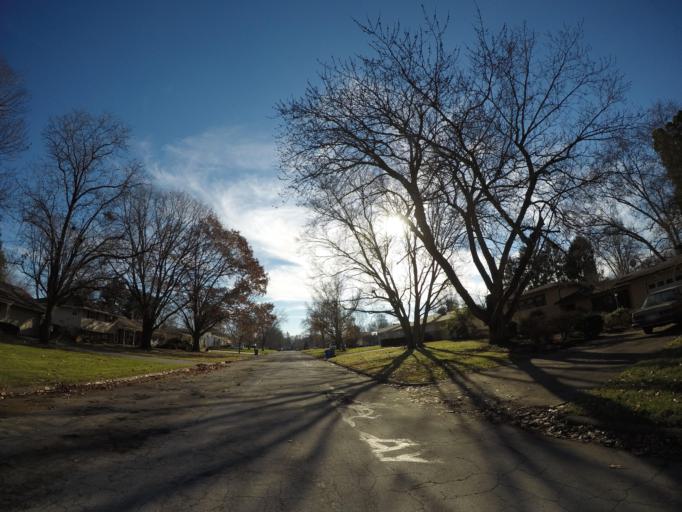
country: US
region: Ohio
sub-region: Franklin County
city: Upper Arlington
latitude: 40.0227
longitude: -83.0500
